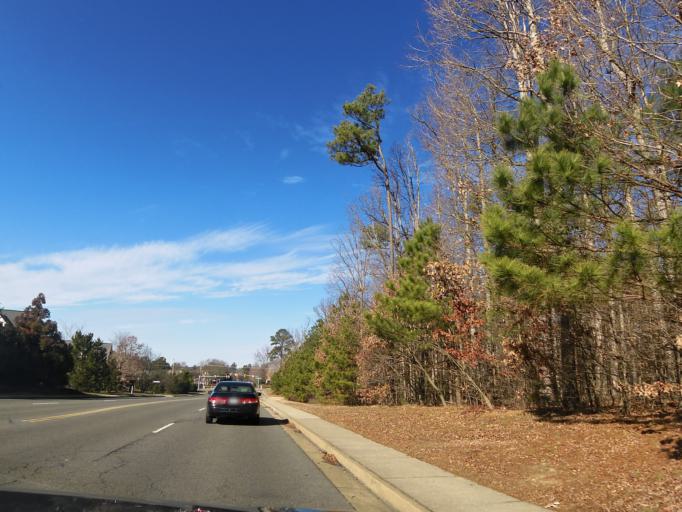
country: US
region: Virginia
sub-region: Henrico County
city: Tuckahoe
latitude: 37.6367
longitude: -77.5619
